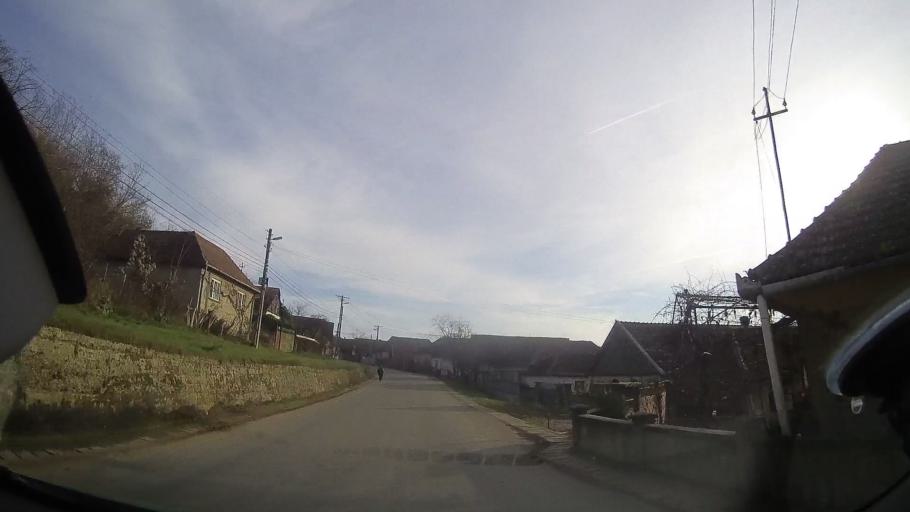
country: RO
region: Bihor
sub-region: Comuna Sarbi
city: Burzuc
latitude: 47.1523
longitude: 22.1724
